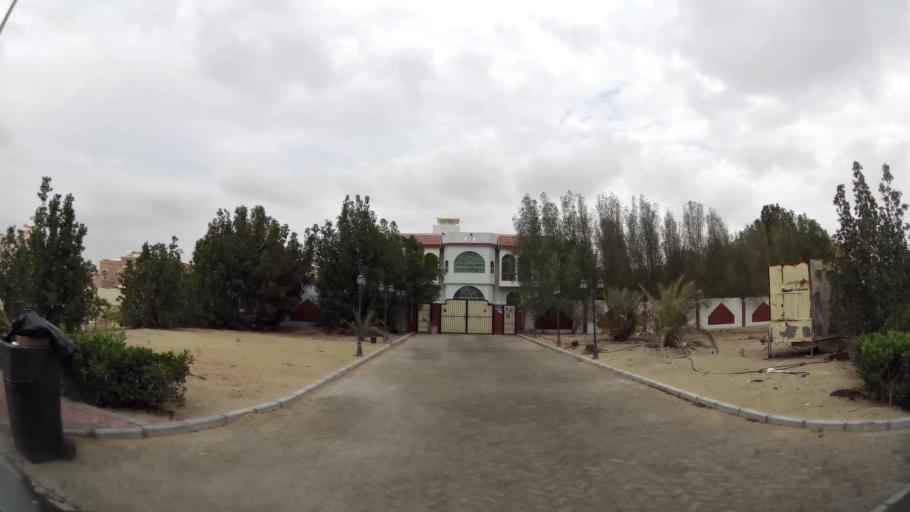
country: AE
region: Abu Dhabi
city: Abu Dhabi
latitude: 24.3514
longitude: 54.6351
